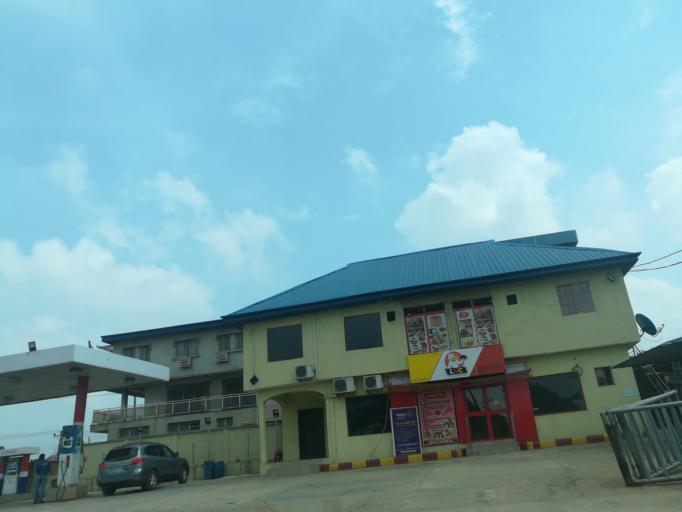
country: NG
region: Lagos
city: Ikorodu
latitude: 6.6128
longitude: 3.5017
